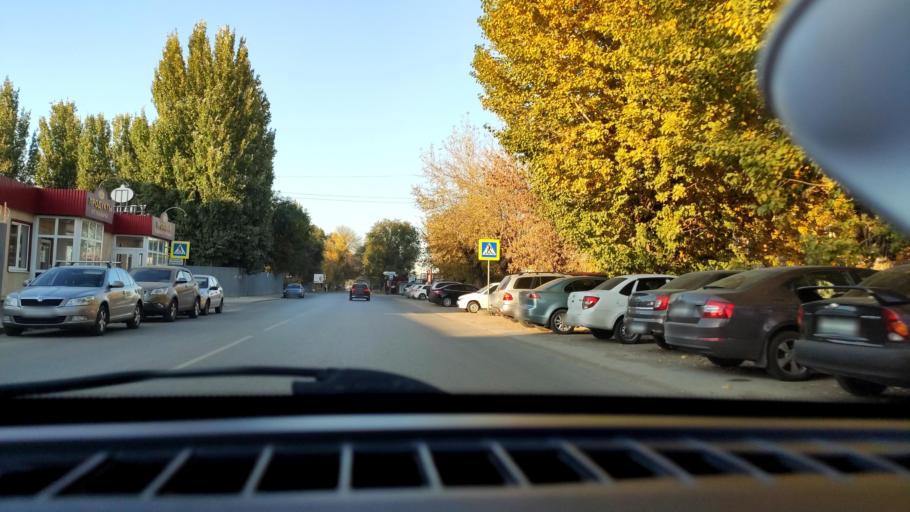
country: RU
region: Samara
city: Samara
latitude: 53.1873
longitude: 50.2449
